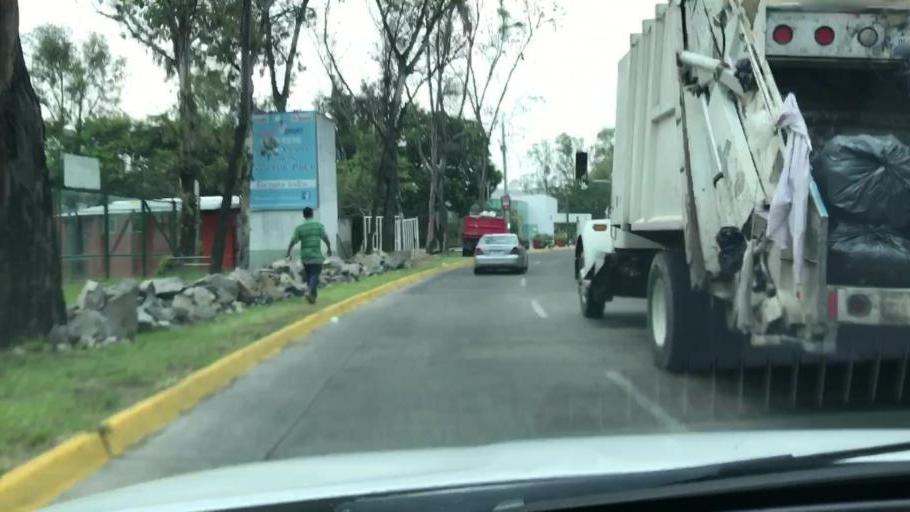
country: MX
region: Jalisco
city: Guadalajara
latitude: 20.6596
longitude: -103.4326
